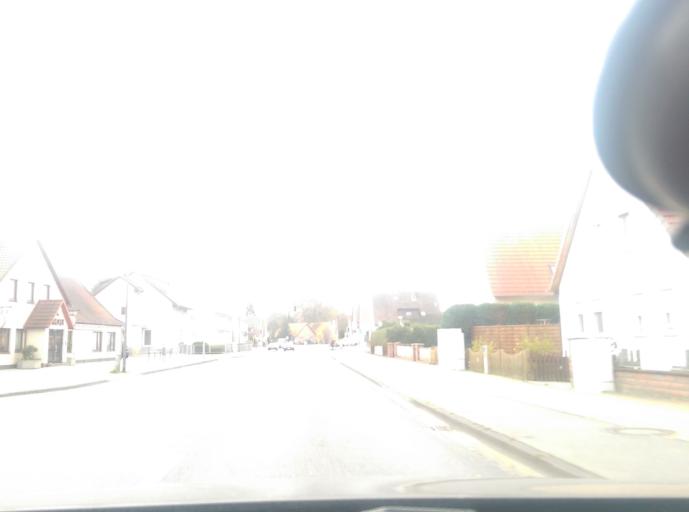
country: DE
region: Lower Saxony
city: Hambuhren
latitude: 52.6059
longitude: 10.0231
